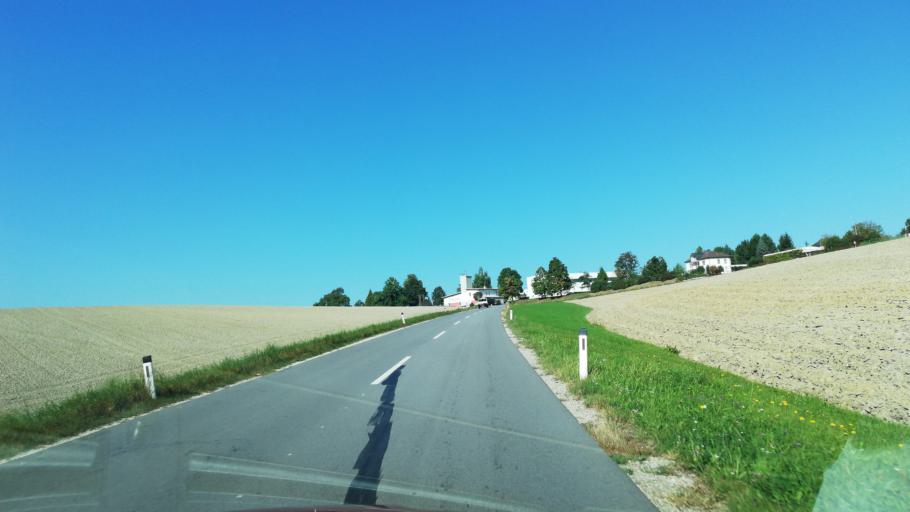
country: AT
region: Upper Austria
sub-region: Politischer Bezirk Grieskirchen
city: Grieskirchen
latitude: 48.2021
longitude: 13.8270
